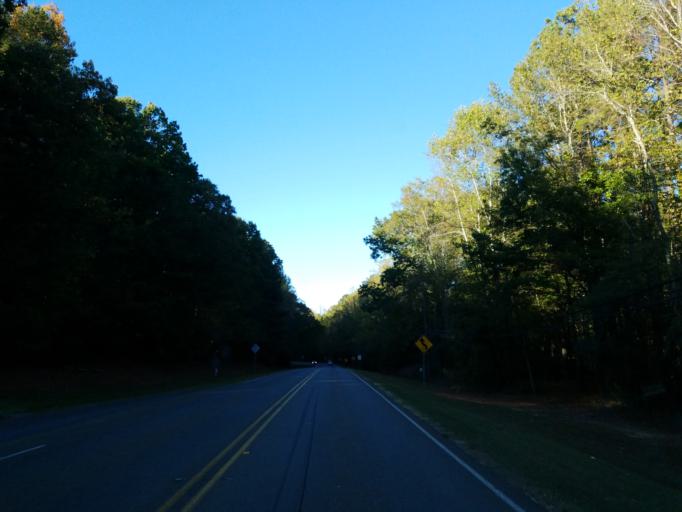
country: US
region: Georgia
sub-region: Pickens County
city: Nelson
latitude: 34.3745
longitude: -84.3718
